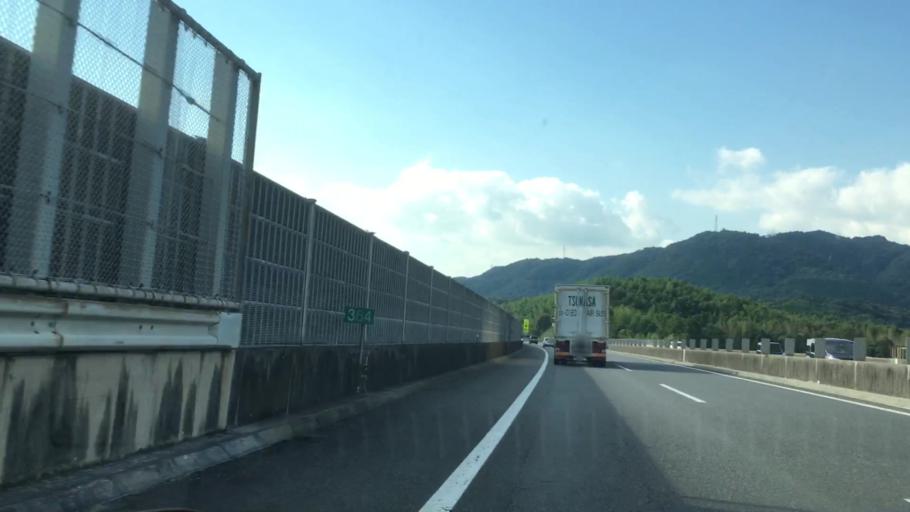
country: JP
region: Yamaguchi
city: Kudamatsu
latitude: 34.0384
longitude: 131.9238
